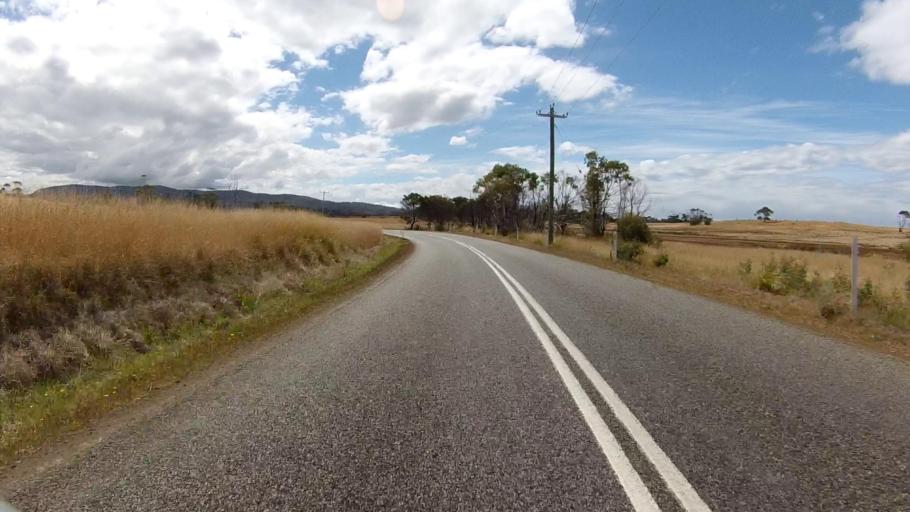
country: AU
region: Tasmania
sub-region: Sorell
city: Sorell
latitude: -42.2768
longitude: 148.0041
